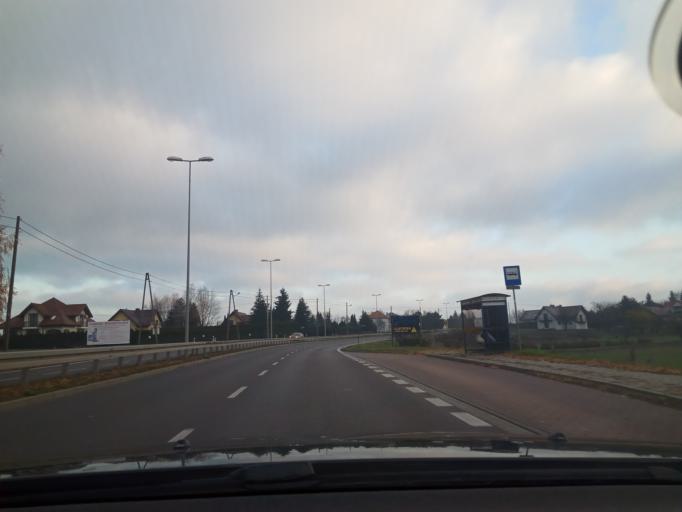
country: PL
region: Lesser Poland Voivodeship
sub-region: Powiat wielicki
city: Wegrzce Wielkie
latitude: 50.1189
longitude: 20.0918
